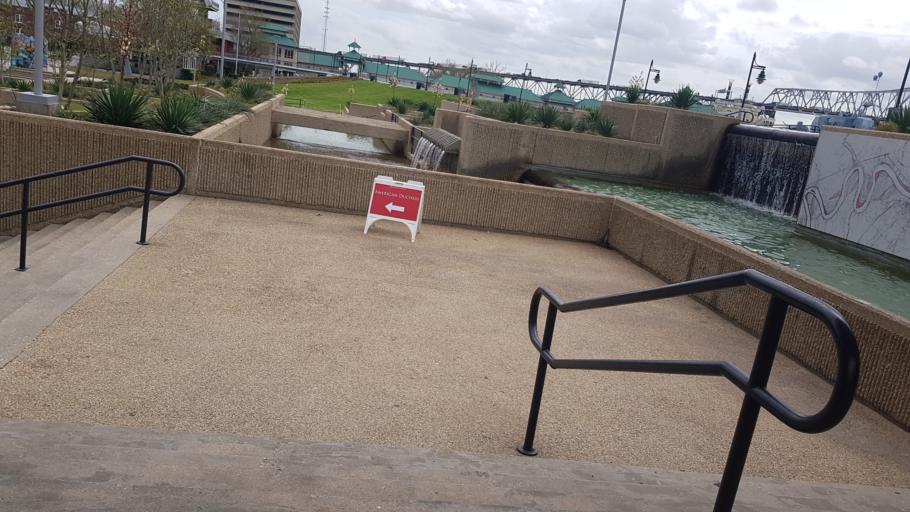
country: US
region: Louisiana
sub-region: West Baton Rouge Parish
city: Port Allen
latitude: 30.4451
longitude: -91.1906
